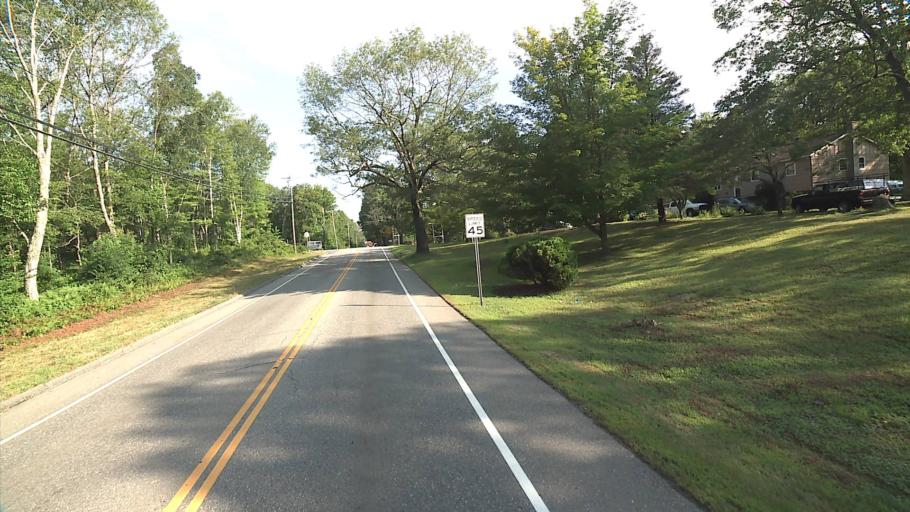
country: US
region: Connecticut
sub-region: New London County
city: Pawcatuck
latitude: 41.4164
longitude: -71.8565
